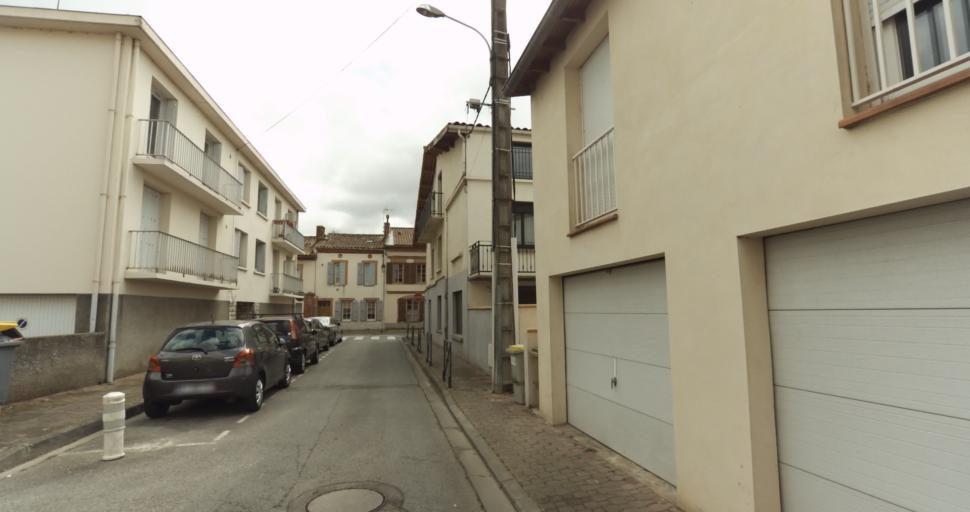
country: FR
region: Midi-Pyrenees
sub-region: Departement de la Haute-Garonne
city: Auterive
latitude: 43.3498
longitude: 1.4736
